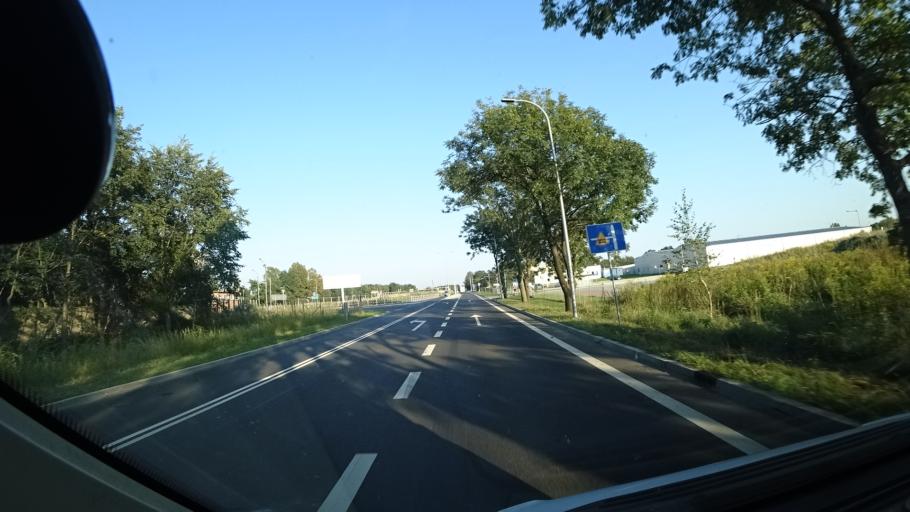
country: PL
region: Opole Voivodeship
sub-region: Powiat kedzierzynsko-kozielski
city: Bierawa
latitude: 50.2910
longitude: 18.2604
